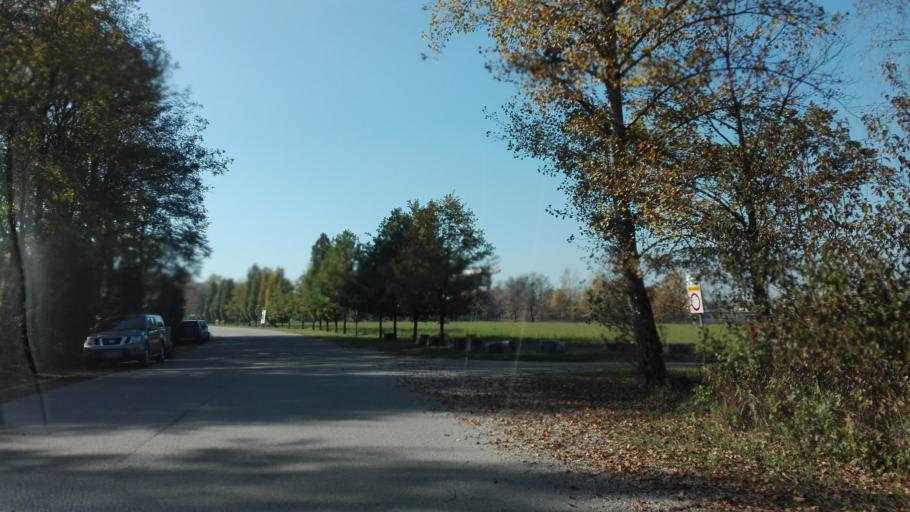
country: AT
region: Upper Austria
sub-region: Politischer Bezirk Urfahr-Umgebung
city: Ottensheim
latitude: 48.3158
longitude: 14.1562
